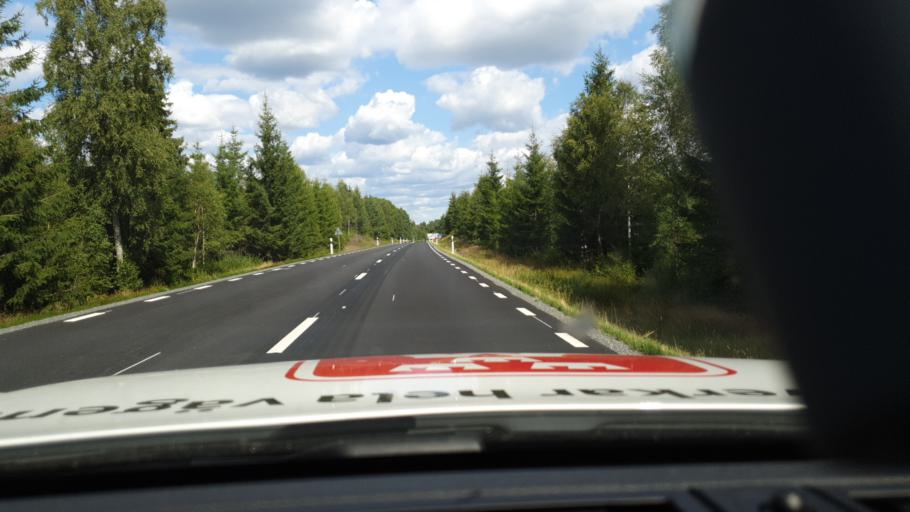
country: SE
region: Joenkoeping
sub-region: Vaggeryds Kommun
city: Skillingaryd
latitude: 57.4108
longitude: 14.0698
